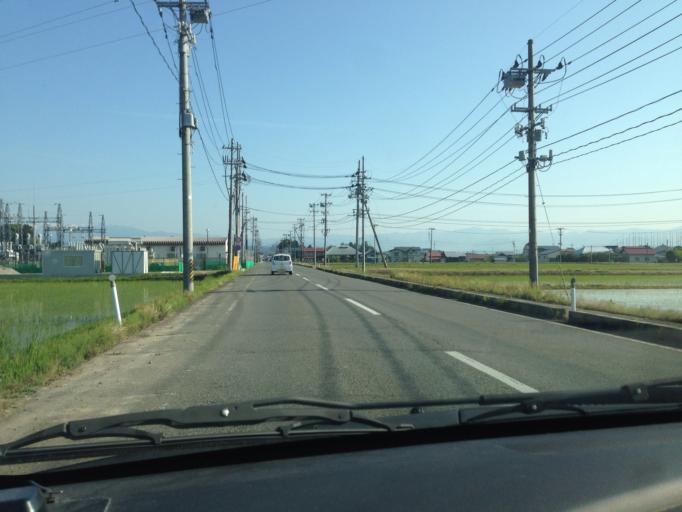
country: JP
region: Fukushima
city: Kitakata
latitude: 37.5502
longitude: 139.8305
